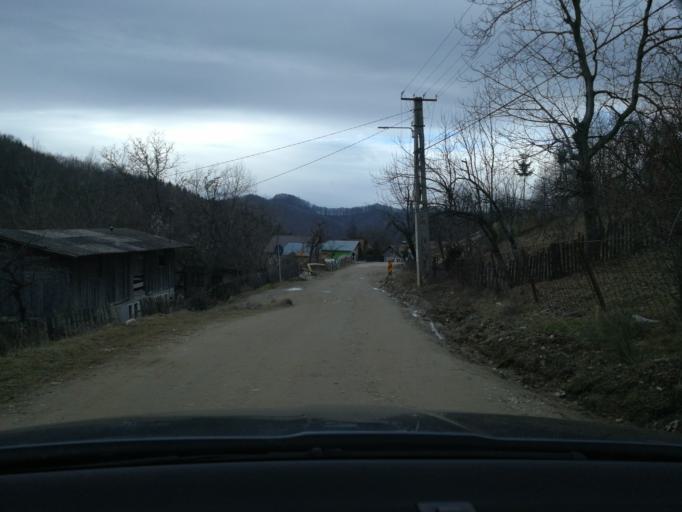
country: RO
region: Dambovita
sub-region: Comuna Bezdead
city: Bezdead
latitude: 45.1673
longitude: 25.5466
